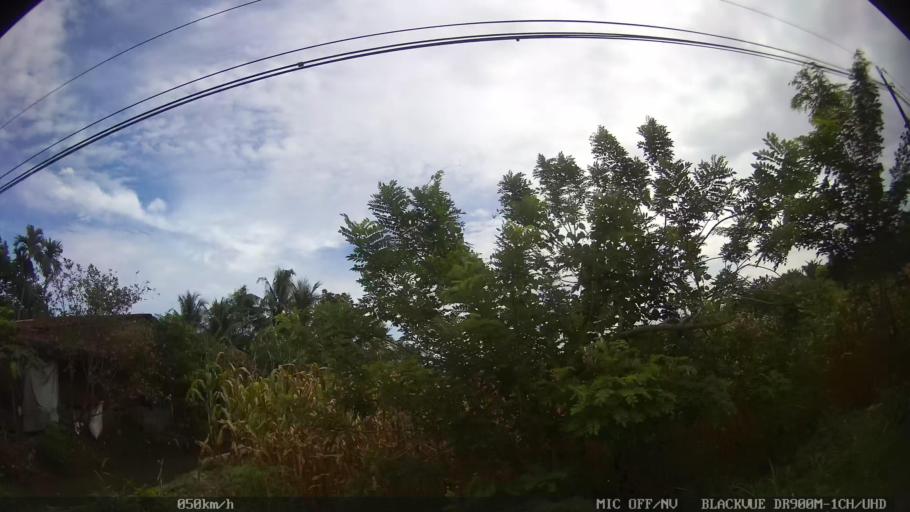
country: ID
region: North Sumatra
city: Sunggal
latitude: 3.5726
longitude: 98.5661
